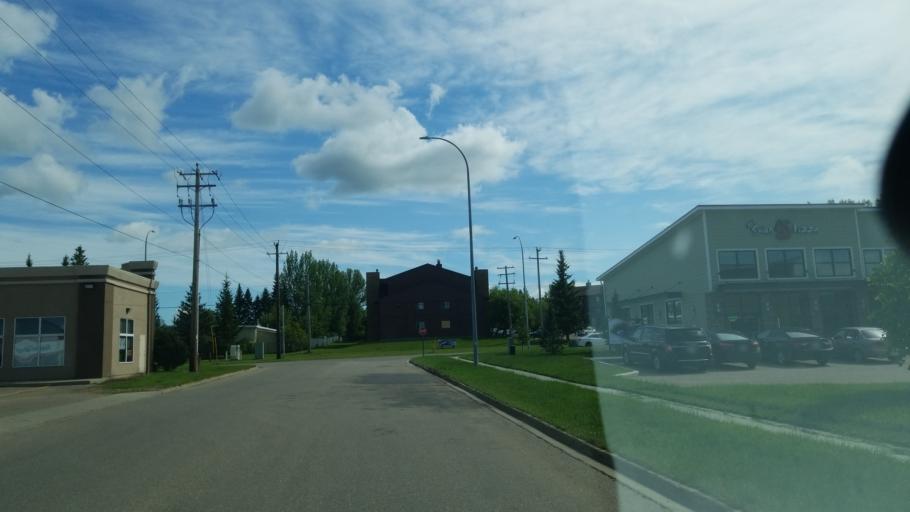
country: CA
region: Saskatchewan
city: Lloydminster
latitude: 53.2714
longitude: -110.0086
